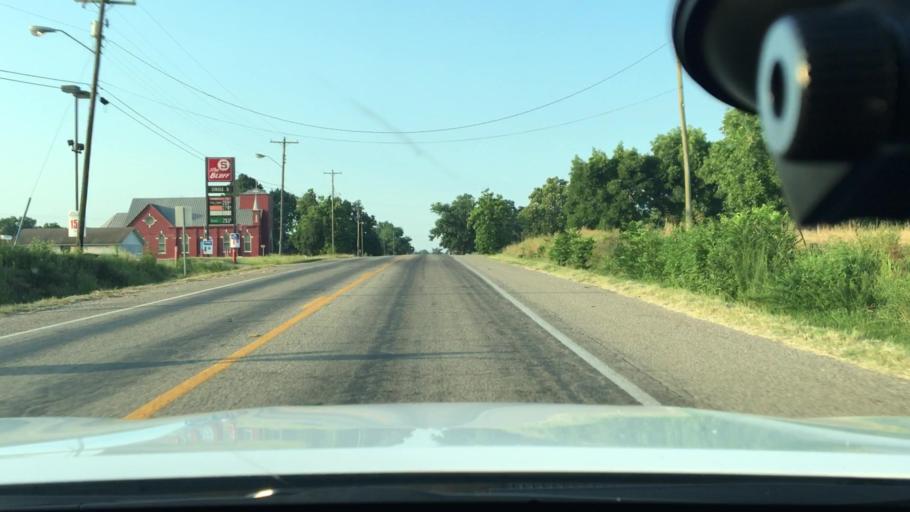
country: US
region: Arkansas
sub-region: Johnson County
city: Clarksville
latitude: 35.3887
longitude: -93.5300
